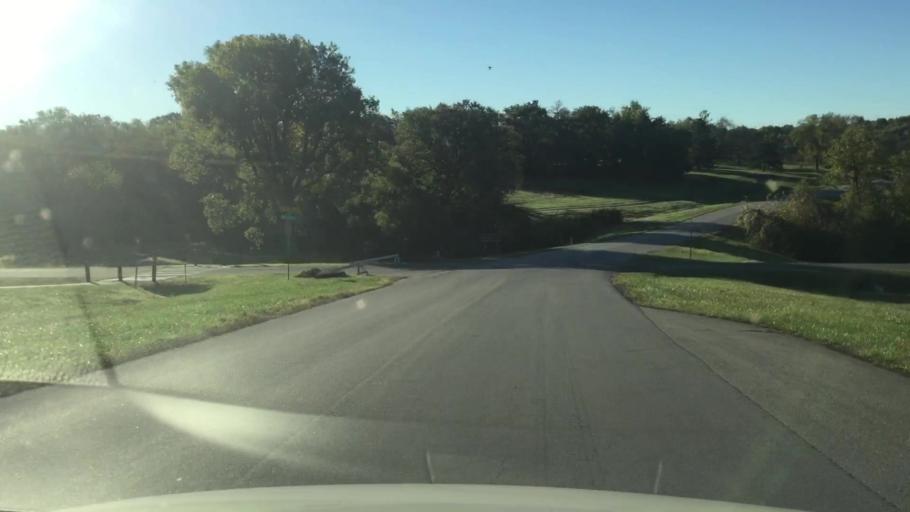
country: US
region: Kansas
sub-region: Johnson County
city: Lenexa
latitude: 38.9876
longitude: -94.7943
